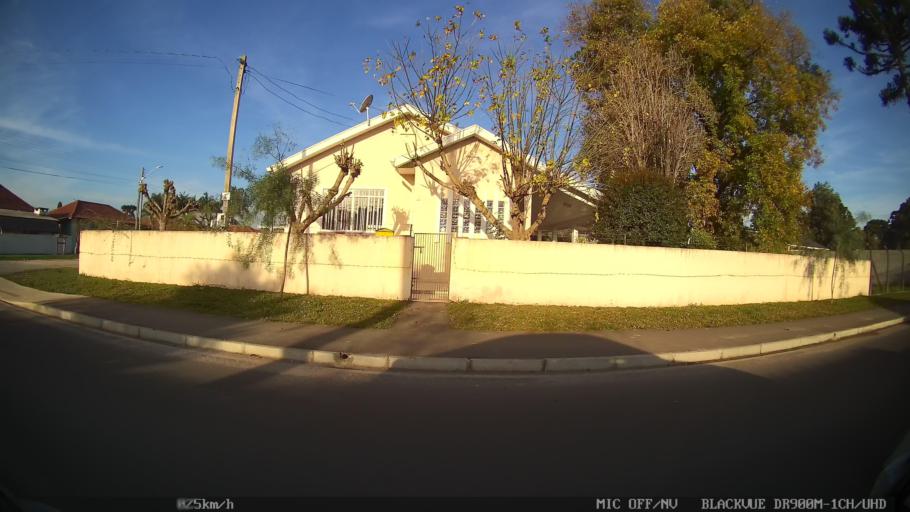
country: BR
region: Parana
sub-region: Pinhais
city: Pinhais
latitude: -25.4620
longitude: -49.1514
